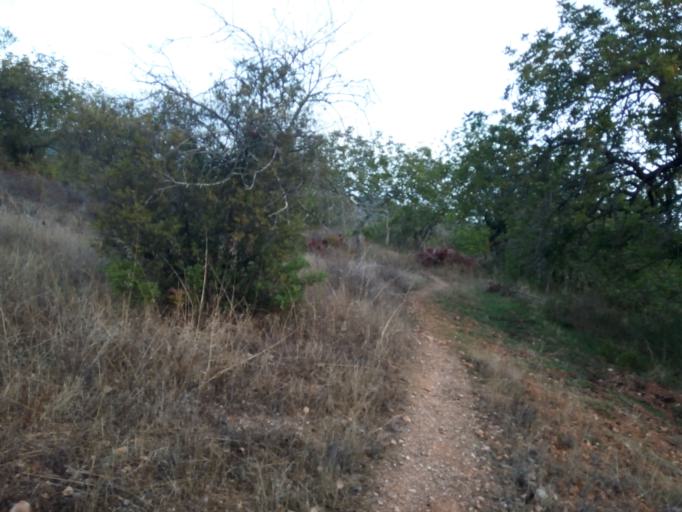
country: PT
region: Faro
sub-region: Faro
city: Santa Barbara de Nexe
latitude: 37.1015
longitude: -7.9557
